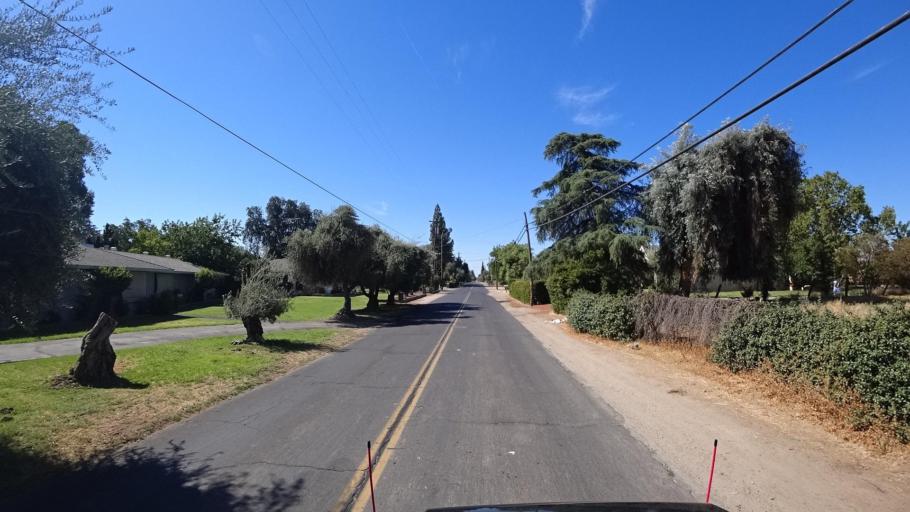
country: US
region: California
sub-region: Fresno County
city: Sunnyside
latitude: 36.7410
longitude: -119.7093
